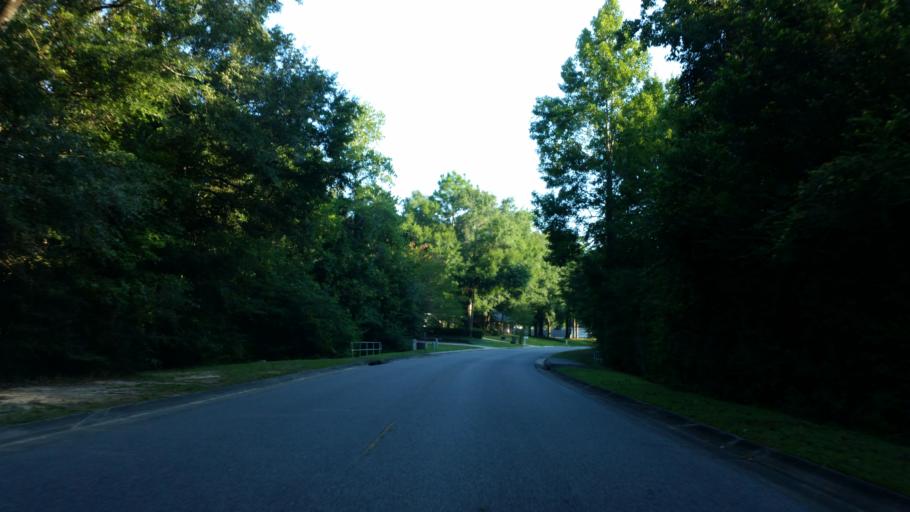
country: US
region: Florida
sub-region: Escambia County
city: Ensley
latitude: 30.5439
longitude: -87.2394
